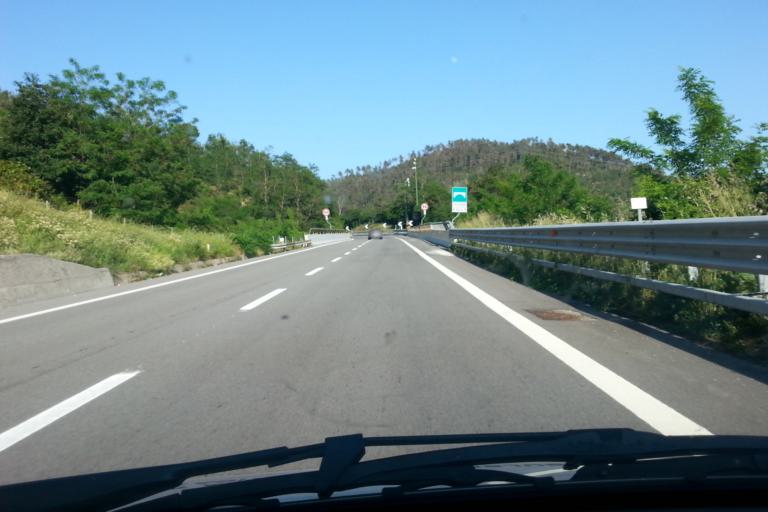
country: IT
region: Liguria
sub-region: Provincia di Savona
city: Quiliano
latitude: 44.2991
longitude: 8.4148
